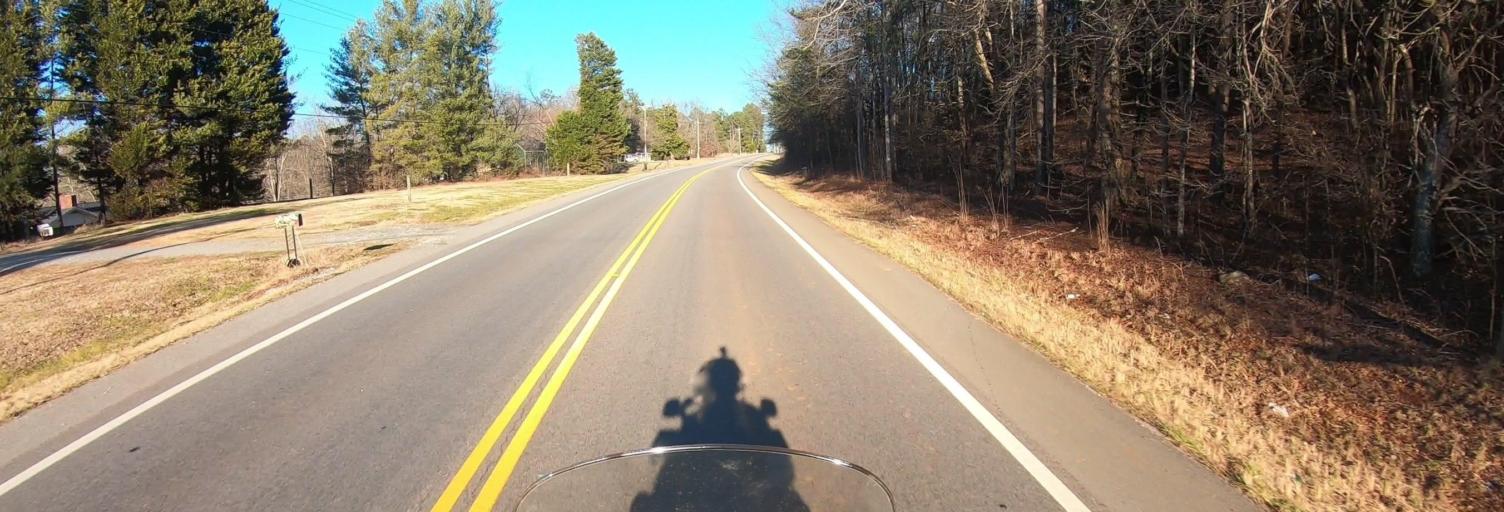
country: US
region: South Carolina
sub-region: Spartanburg County
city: Mayo
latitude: 35.1568
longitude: -81.9291
